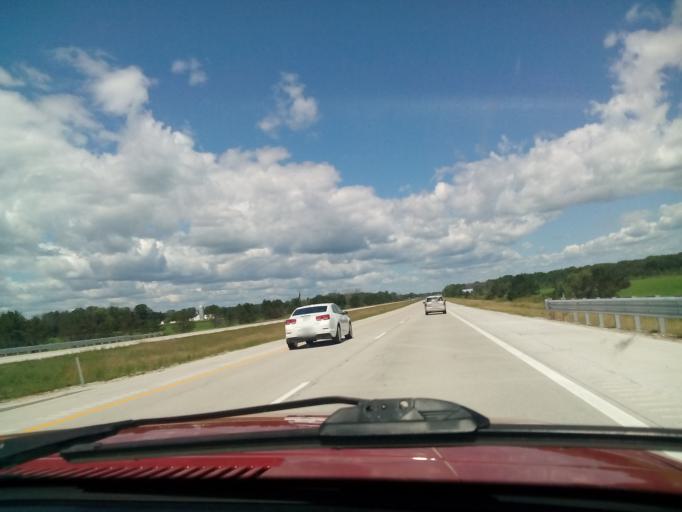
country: US
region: Michigan
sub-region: Bay County
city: Pinconning
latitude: 43.8992
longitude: -84.0199
